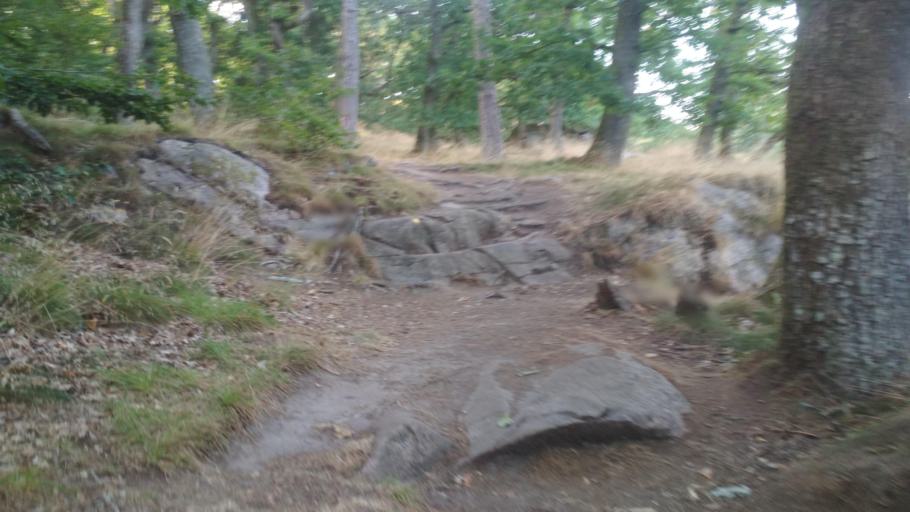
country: DK
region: Capital Region
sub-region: Bornholm Kommune
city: Akirkeby
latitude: 55.1115
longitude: 14.9044
